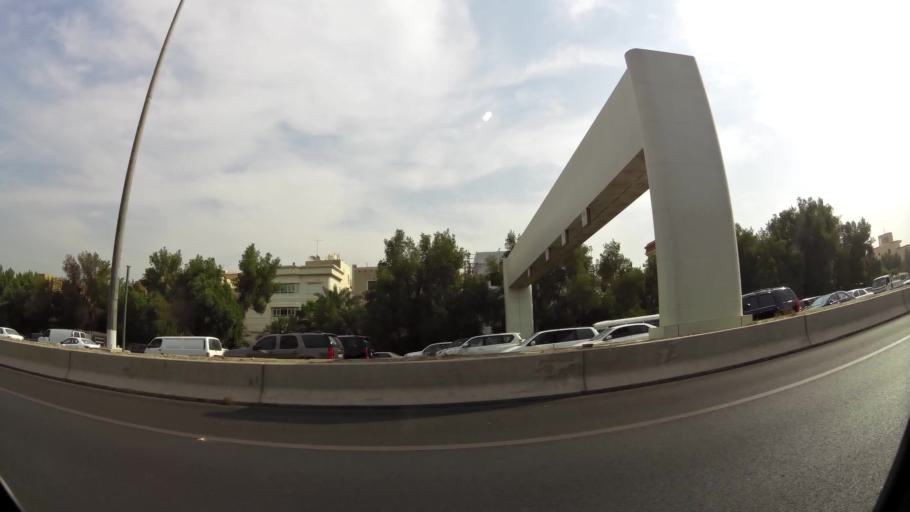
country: KW
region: Al Asimah
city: Ash Shamiyah
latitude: 29.3131
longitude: 47.9762
